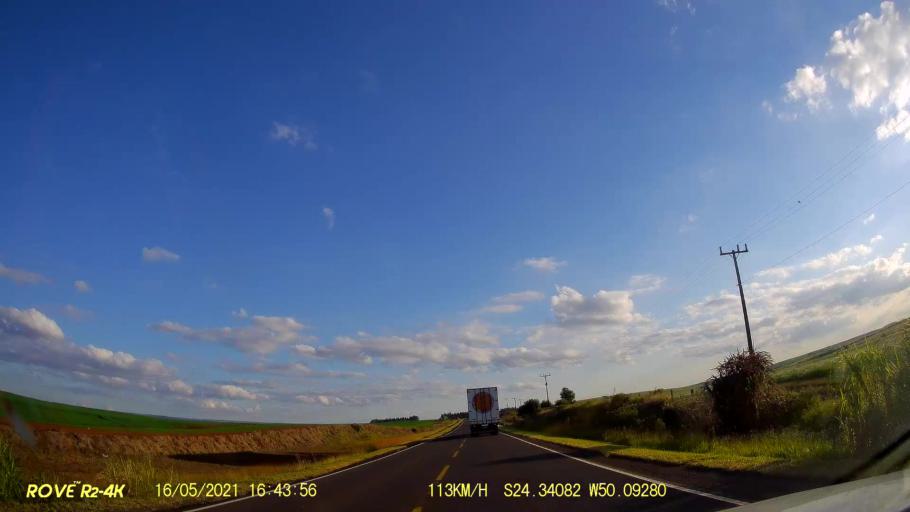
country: BR
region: Parana
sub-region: Pirai Do Sul
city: Pirai do Sul
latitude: -24.3413
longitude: -50.0929
